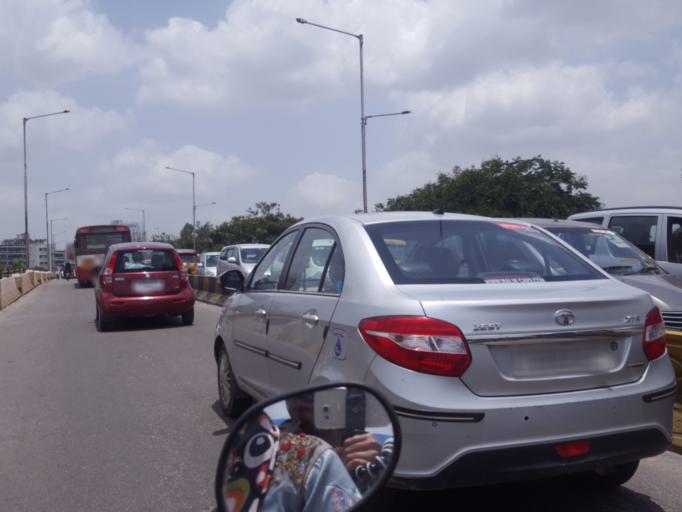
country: IN
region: Telangana
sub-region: Hyderabad
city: Hyderabad
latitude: 17.4010
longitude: 78.4513
